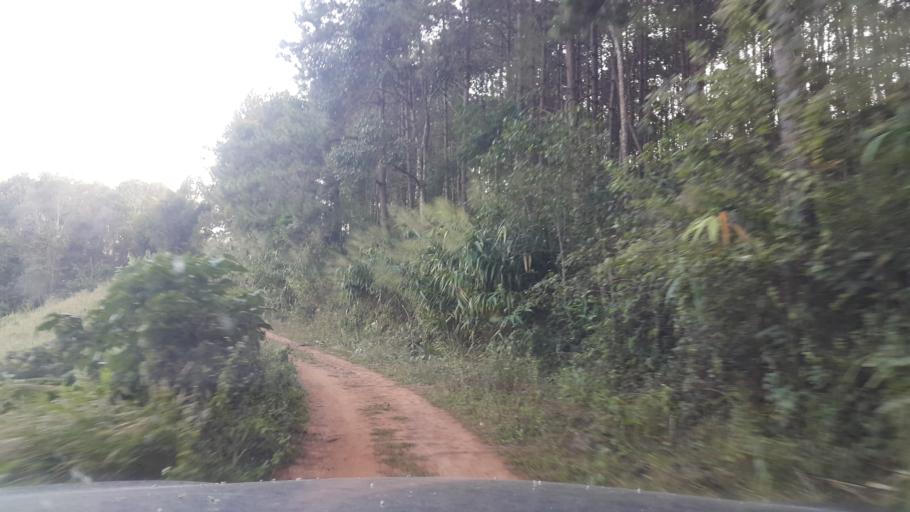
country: TH
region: Chiang Mai
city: Samoeng
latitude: 19.0144
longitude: 98.6499
